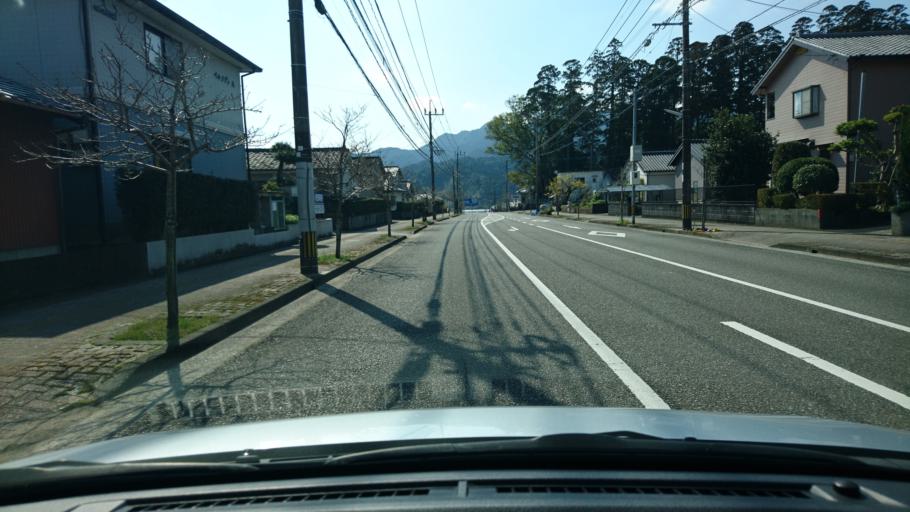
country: JP
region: Miyazaki
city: Miyazaki-shi
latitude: 31.8276
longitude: 131.4201
